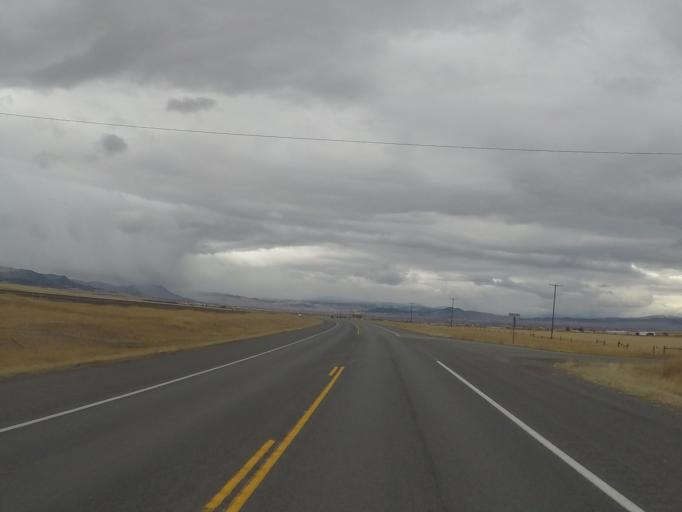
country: US
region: Montana
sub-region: Lewis and Clark County
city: East Helena
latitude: 46.5823
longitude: -111.8510
